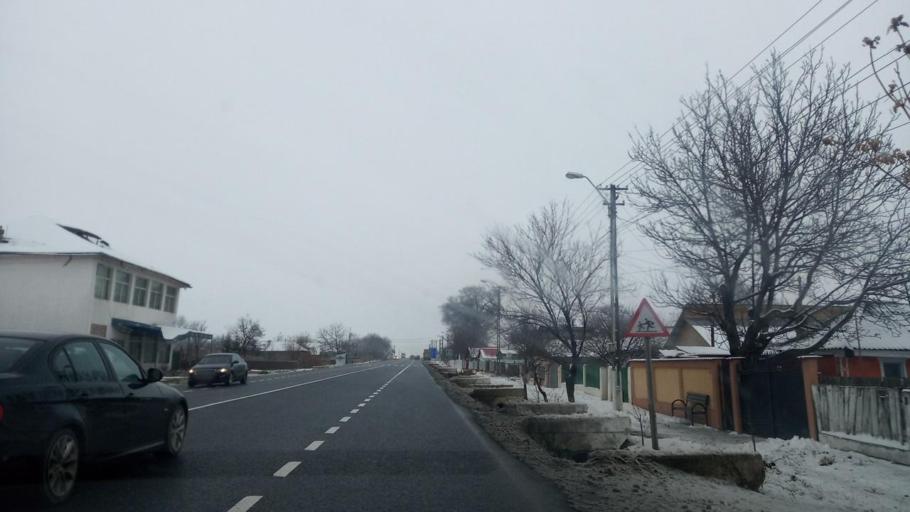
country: RO
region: Vrancea
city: Marasheshty
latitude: 45.9182
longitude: 27.2092
